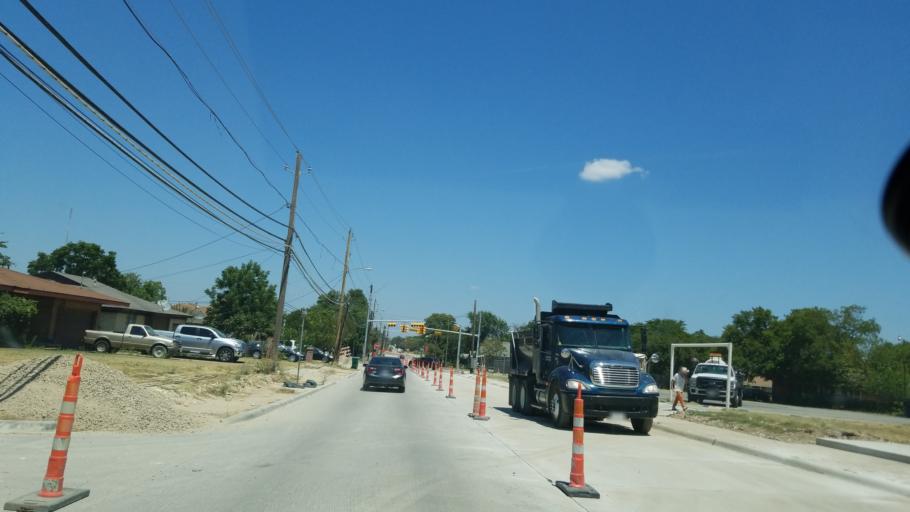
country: US
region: Texas
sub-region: Dallas County
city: Cockrell Hill
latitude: 32.7341
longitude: -96.8915
